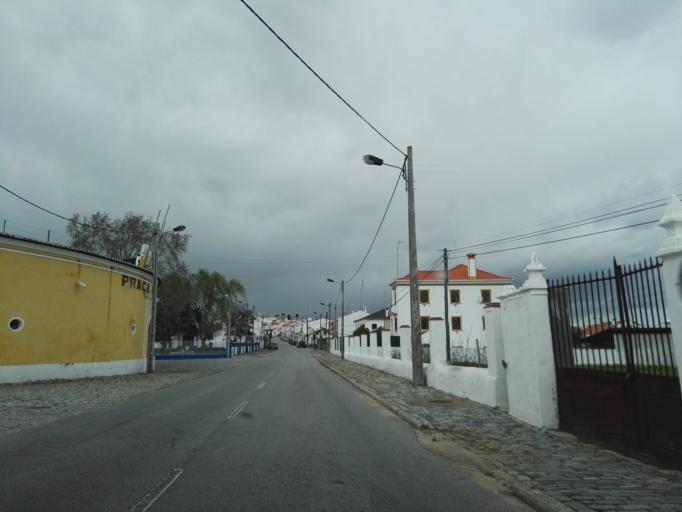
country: PT
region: Portalegre
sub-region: Arronches
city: Arronches
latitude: 39.0025
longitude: -7.2472
